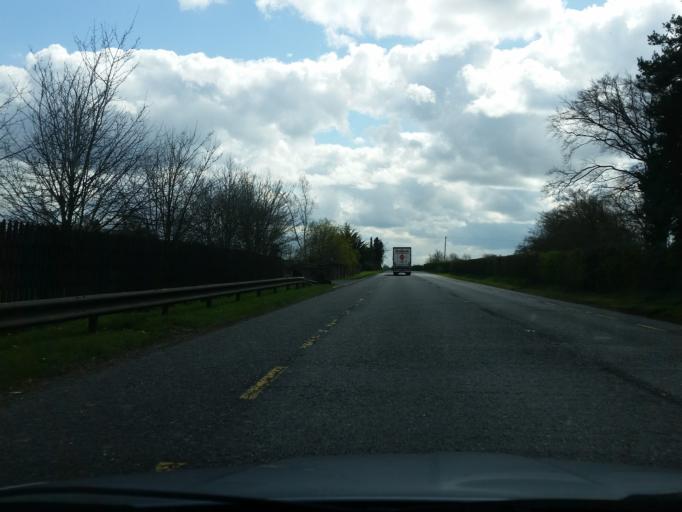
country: IE
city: Kentstown
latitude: 53.6177
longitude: -6.4822
